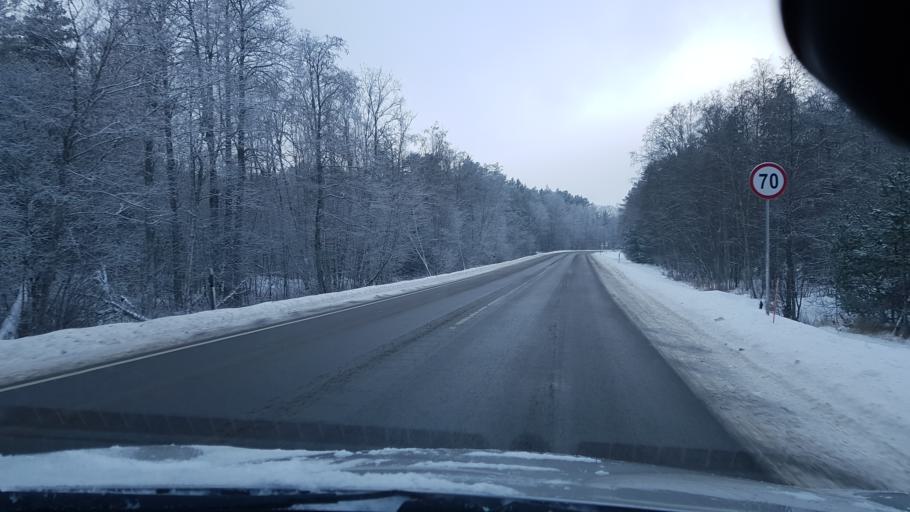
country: EE
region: Harju
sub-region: Keila linn
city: Keila
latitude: 59.3372
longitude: 24.2500
